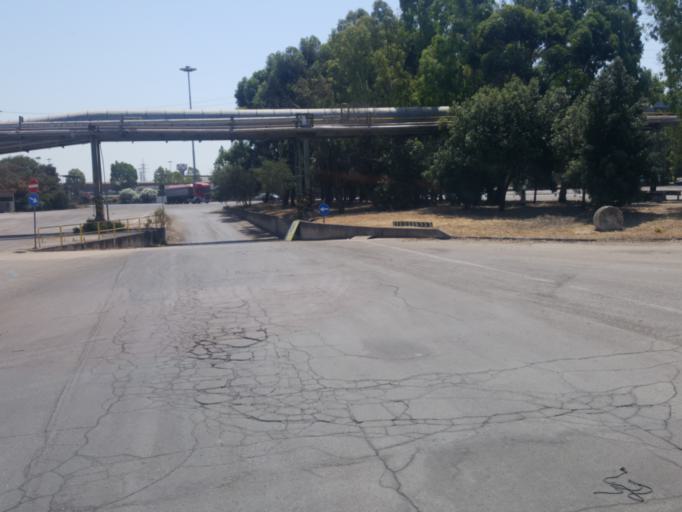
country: IT
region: Apulia
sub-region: Provincia di Taranto
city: Statte
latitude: 40.5159
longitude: 17.1887
